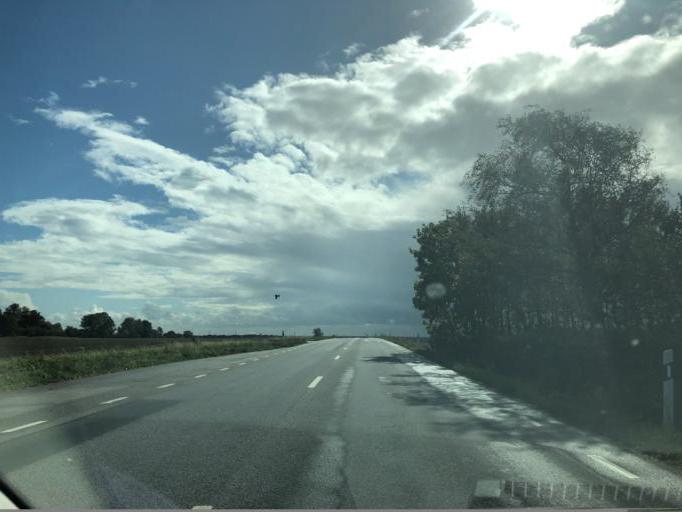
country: SE
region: Skane
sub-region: Helsingborg
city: Glumslov
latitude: 55.9190
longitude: 12.8162
